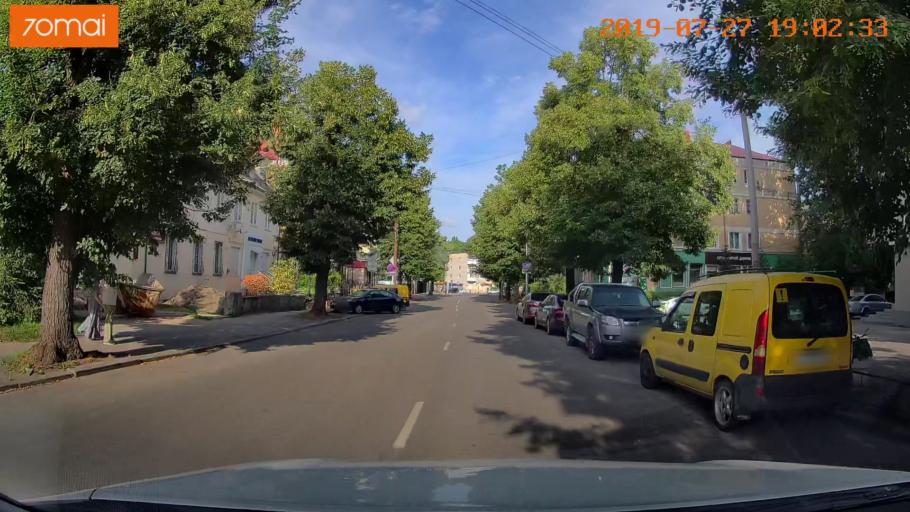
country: RU
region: Kaliningrad
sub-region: Gorod Kaliningrad
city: Kaliningrad
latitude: 54.7246
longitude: 20.4956
